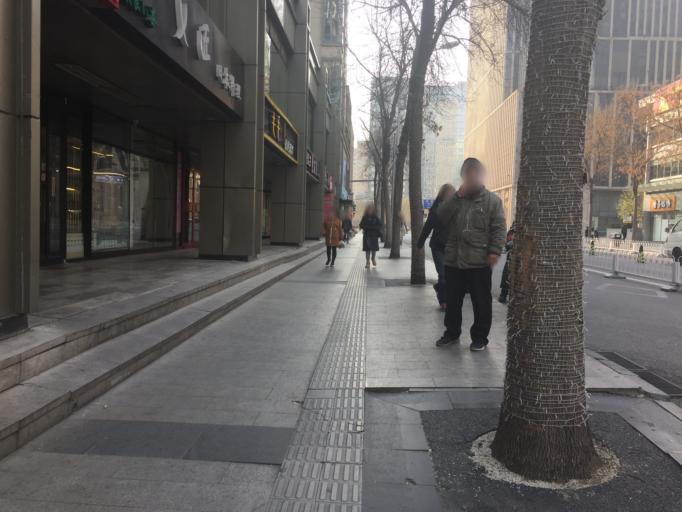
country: CN
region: Beijing
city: Chaowai
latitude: 39.9094
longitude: 116.4655
